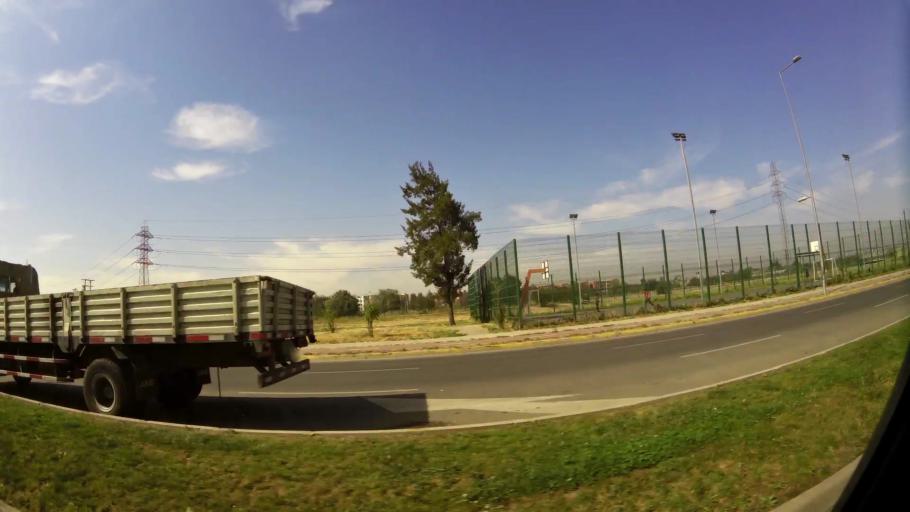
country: CL
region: Santiago Metropolitan
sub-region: Provincia de Santiago
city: Lo Prado
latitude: -33.4832
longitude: -70.7413
